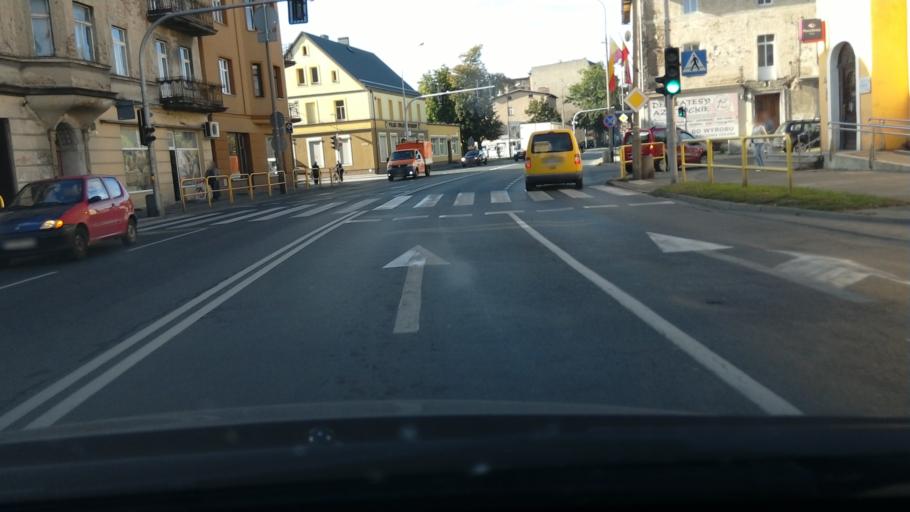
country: PL
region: Lower Silesian Voivodeship
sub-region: Jelenia Gora
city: Jelenia Gora
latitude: 50.8947
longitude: 15.7275
